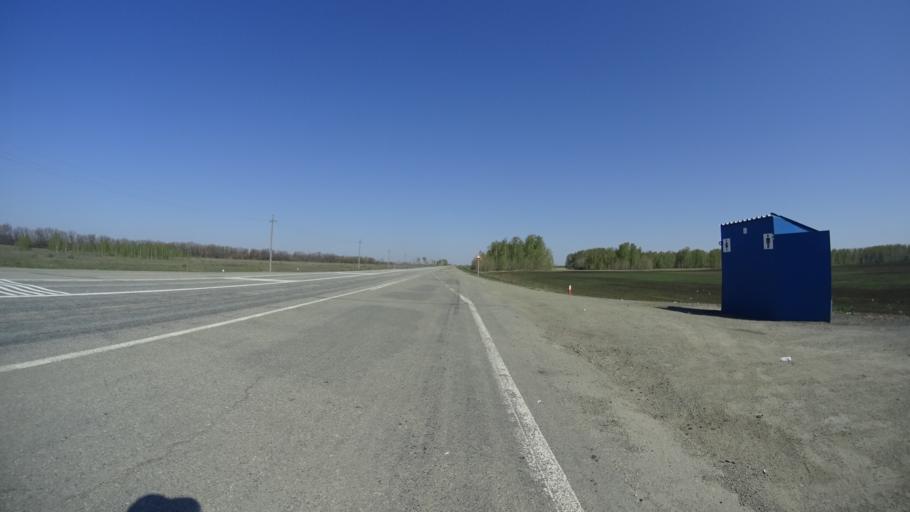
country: RU
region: Chelyabinsk
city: Troitsk
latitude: 54.1882
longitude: 61.4339
